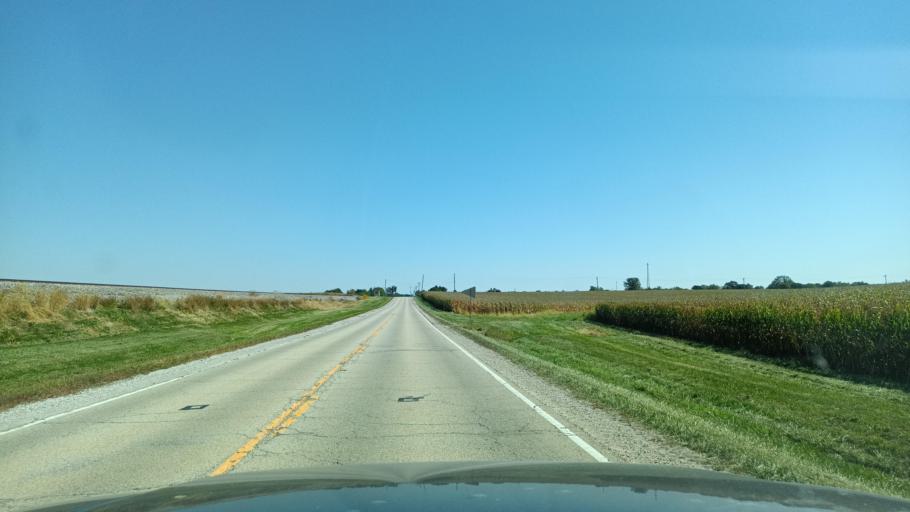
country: US
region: Illinois
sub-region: Tazewell County
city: Mackinaw
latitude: 40.6266
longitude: -89.3127
